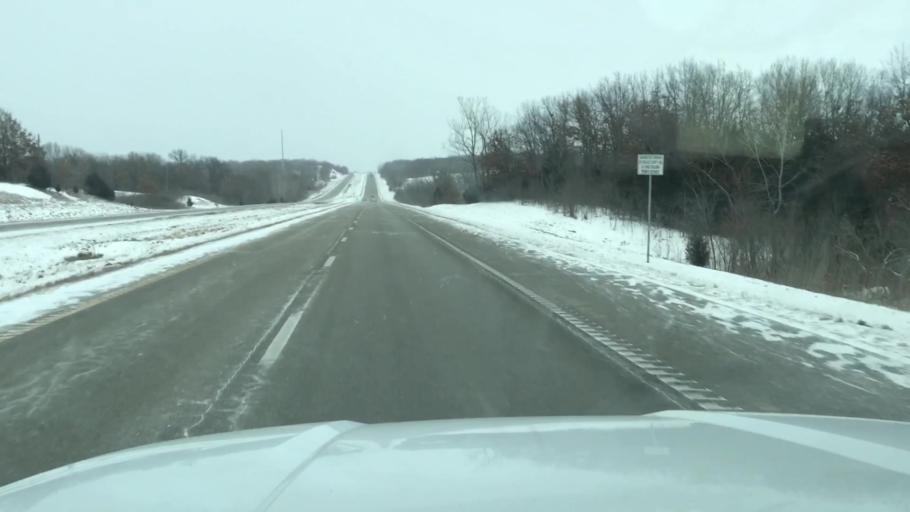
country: US
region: Missouri
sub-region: Clinton County
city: Gower
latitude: 39.7485
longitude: -94.6018
